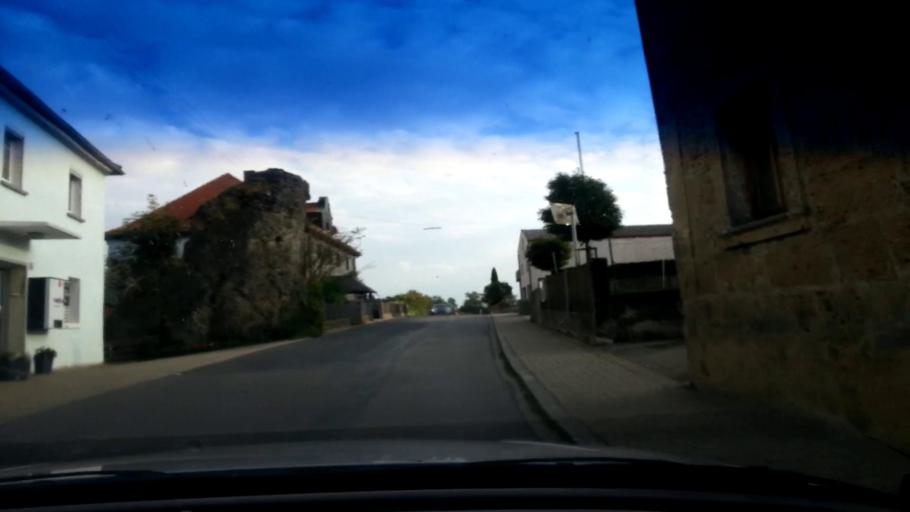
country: DE
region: Bavaria
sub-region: Upper Franconia
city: Wattendorf
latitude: 50.0031
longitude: 11.1348
